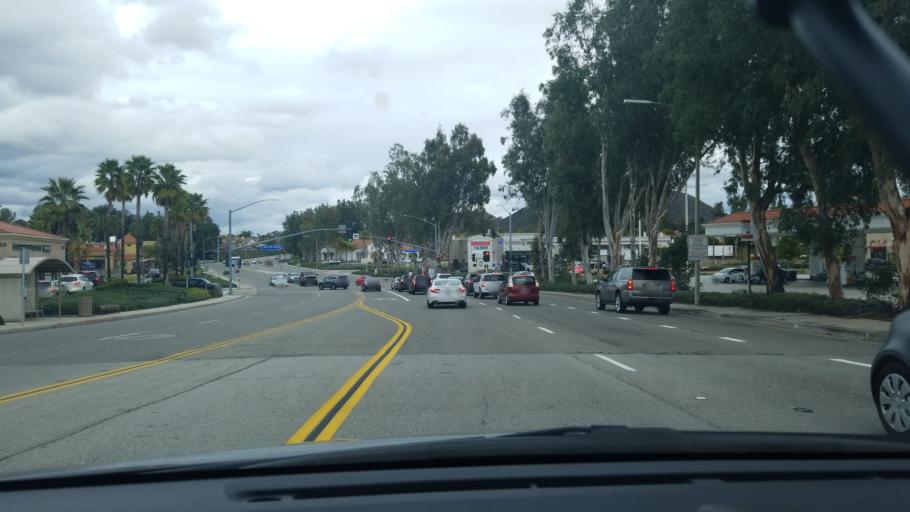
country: US
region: California
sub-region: Riverside County
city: Murrieta Hot Springs
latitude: 33.5739
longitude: -117.1788
